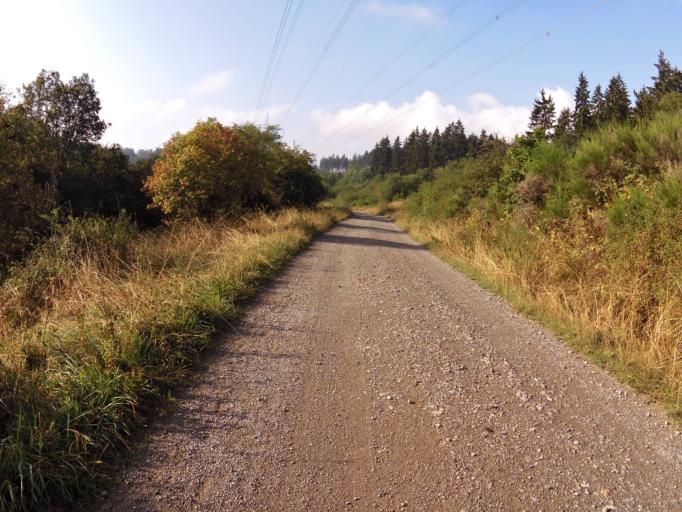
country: DE
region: North Rhine-Westphalia
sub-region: Regierungsbezirk Koln
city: Nettersheim
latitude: 50.4684
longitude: 6.6125
